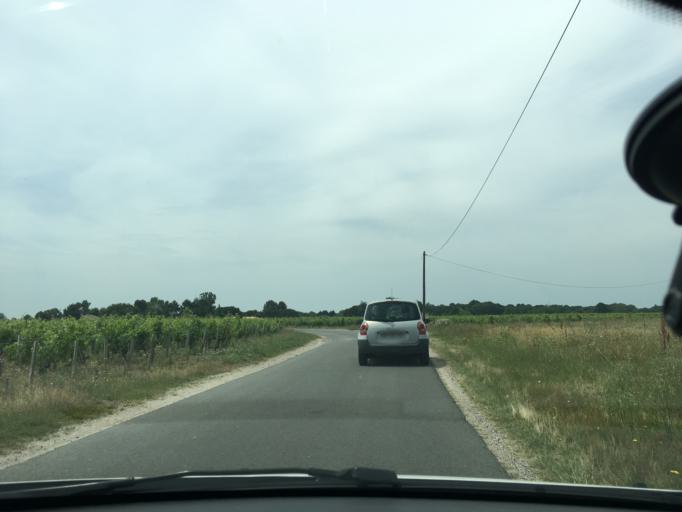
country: FR
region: Aquitaine
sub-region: Departement de la Gironde
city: Listrac-Medoc
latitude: 45.0667
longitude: -0.7973
